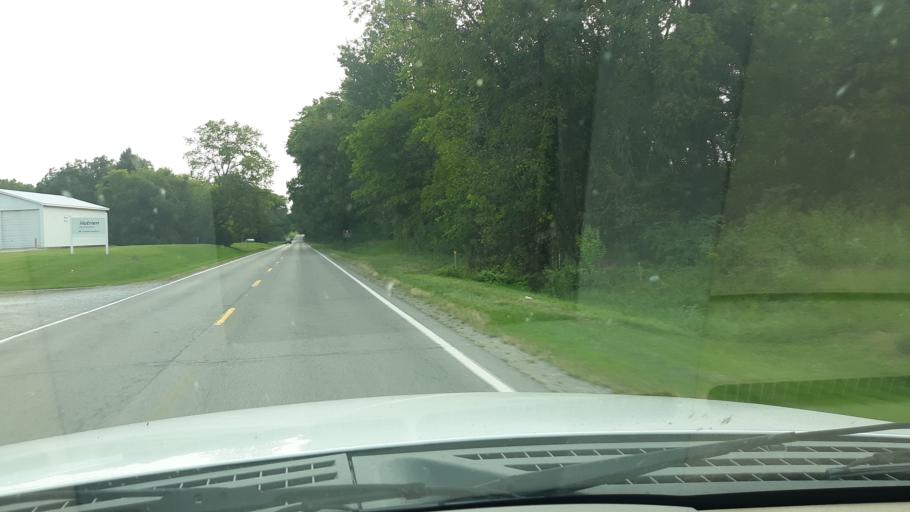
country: US
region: Illinois
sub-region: Wabash County
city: Mount Carmel
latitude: 38.3990
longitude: -87.7970
